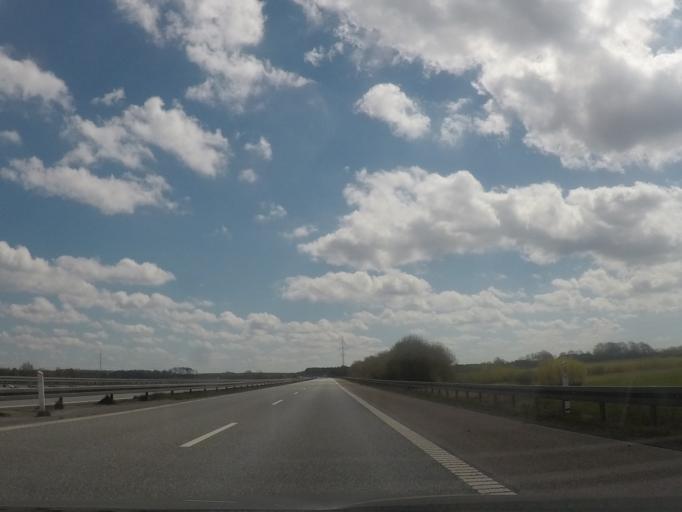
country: DK
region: South Denmark
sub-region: Kolding Kommune
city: Kolding
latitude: 55.5380
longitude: 9.5022
